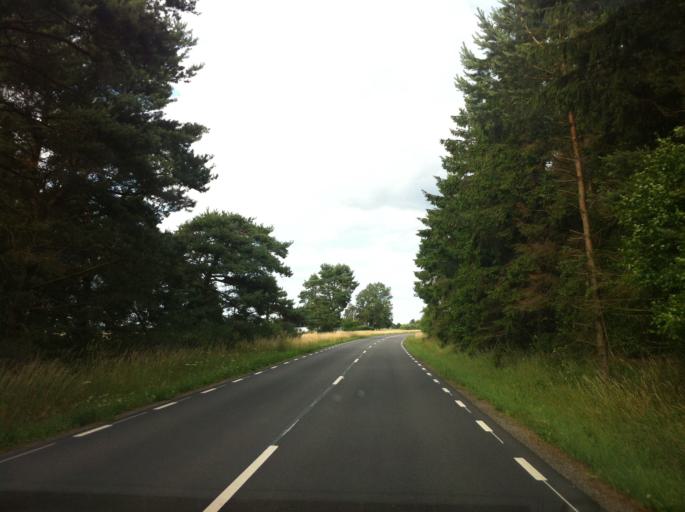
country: SE
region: Skane
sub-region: Simrishamns Kommun
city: Simrishamn
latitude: 55.3930
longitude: 14.1711
